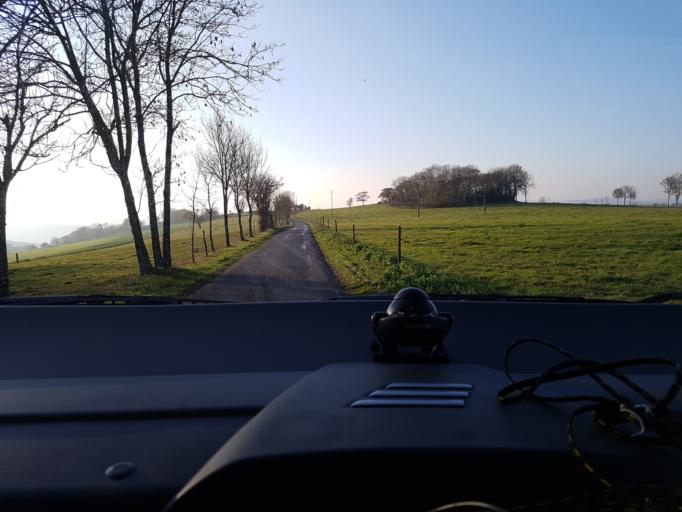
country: FR
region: Lower Normandy
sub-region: Departement du Calvados
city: Clecy
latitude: 48.9162
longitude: -0.4236
